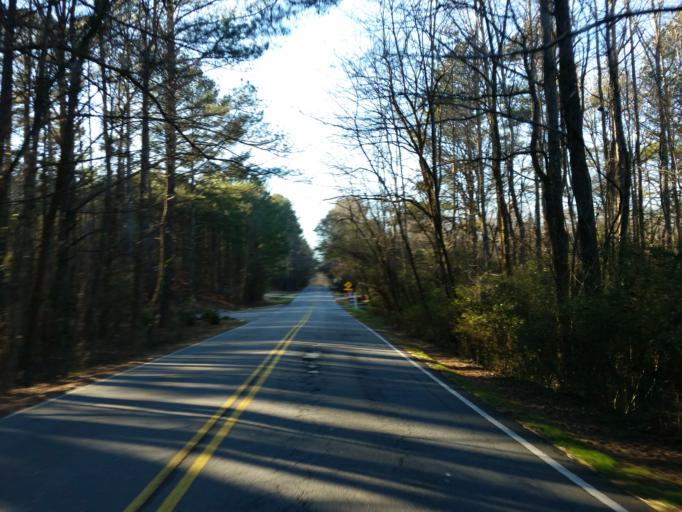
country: US
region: Georgia
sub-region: Cobb County
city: Marietta
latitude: 33.9639
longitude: -84.5977
